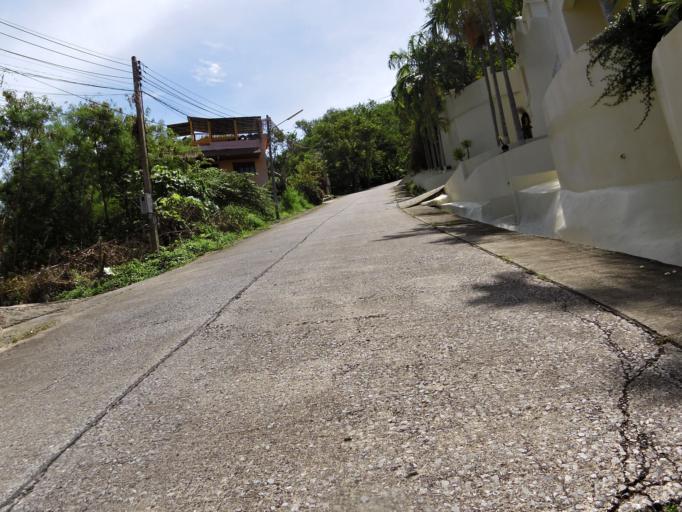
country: TH
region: Phuket
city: Ban Karon
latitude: 7.8471
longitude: 98.3012
